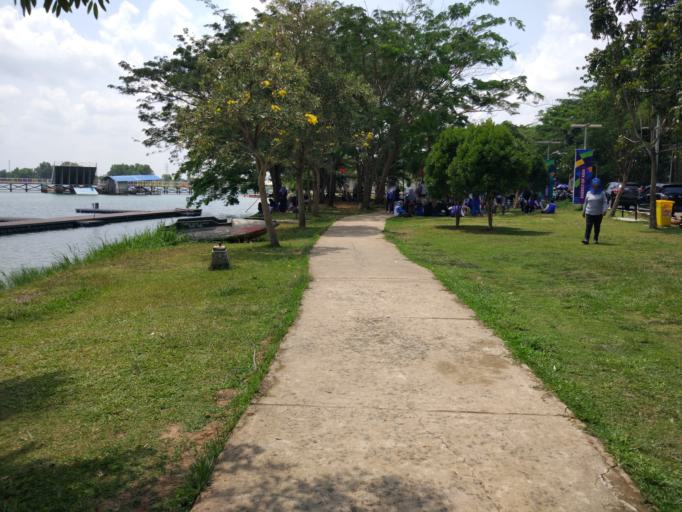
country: ID
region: South Sumatra
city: Plaju
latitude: -3.0181
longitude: 104.7944
